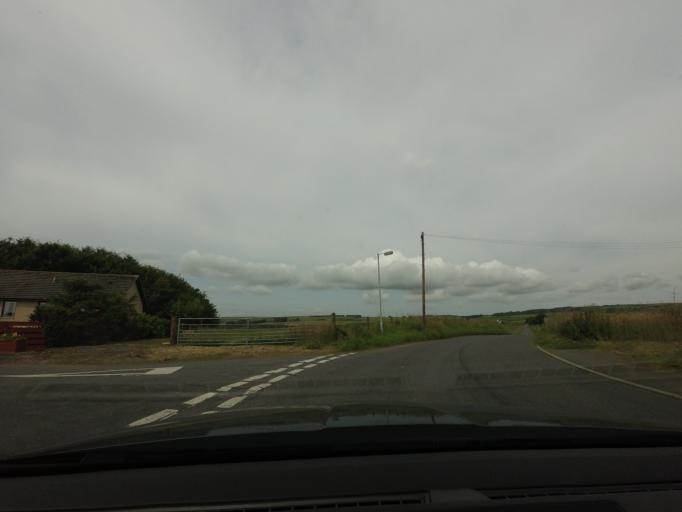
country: GB
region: Scotland
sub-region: Aberdeenshire
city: Turriff
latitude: 57.5773
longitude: -2.2996
